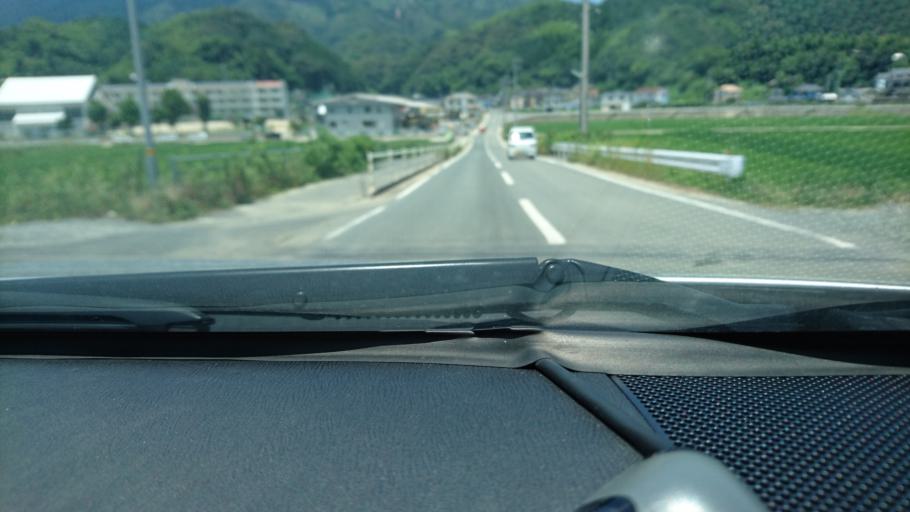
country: JP
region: Ehime
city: Ozu
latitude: 33.5066
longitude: 132.5295
